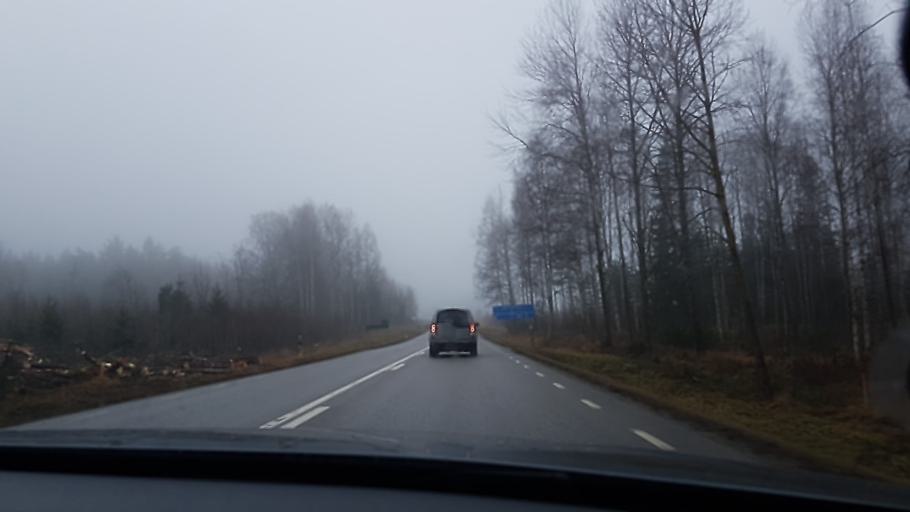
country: SE
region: Vaestra Goetaland
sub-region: Gullspangs Kommun
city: Gullspang
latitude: 58.9653
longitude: 14.0637
